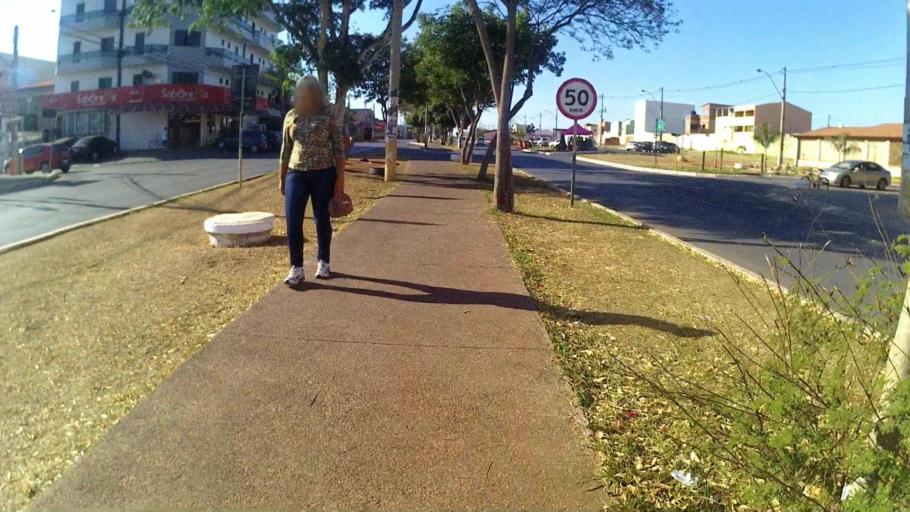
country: BR
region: Federal District
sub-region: Brasilia
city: Brasilia
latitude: -15.9001
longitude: -48.0510
